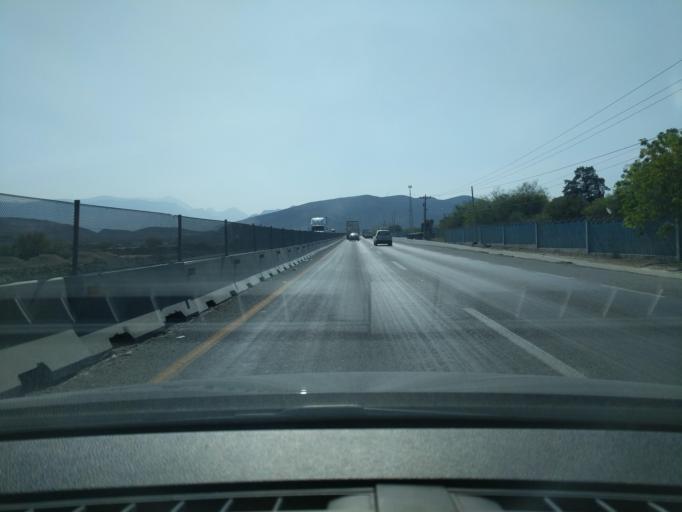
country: MX
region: Nuevo Leon
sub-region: Garcia
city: Los Parques
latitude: 25.7692
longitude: -100.4803
